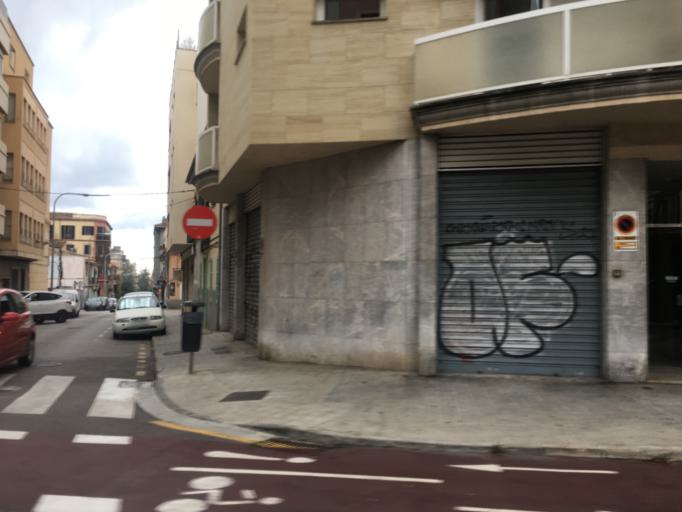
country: ES
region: Balearic Islands
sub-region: Illes Balears
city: Palma
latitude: 39.5737
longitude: 2.6396
